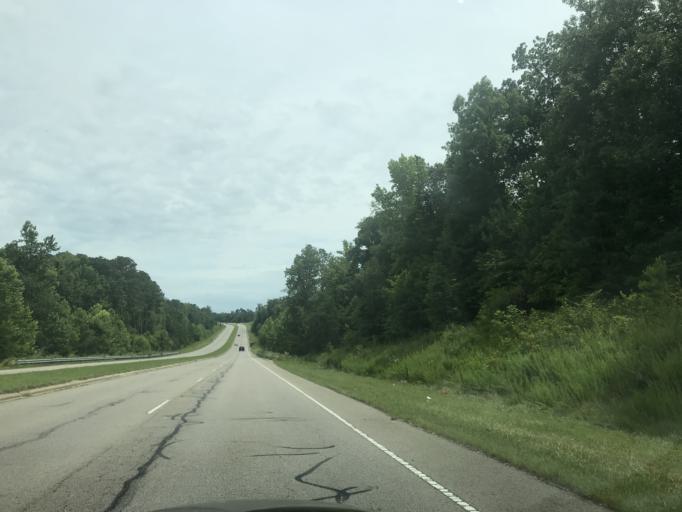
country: US
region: North Carolina
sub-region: Vance County
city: South Henderson
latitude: 36.3156
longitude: -78.4470
